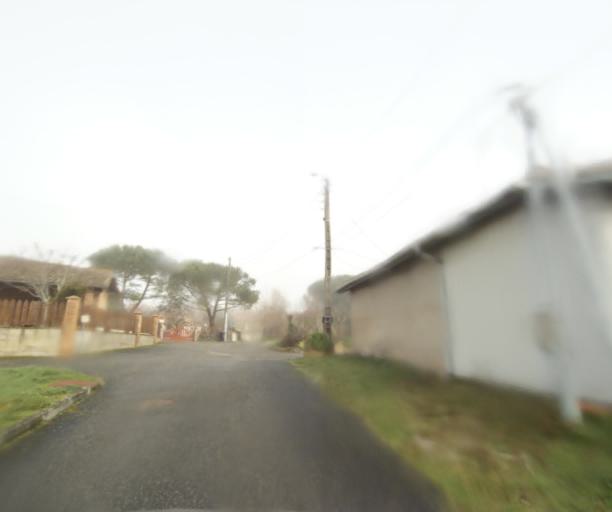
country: FR
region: Midi-Pyrenees
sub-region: Departement de la Haute-Garonne
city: Villaudric
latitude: 43.8201
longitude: 1.4603
